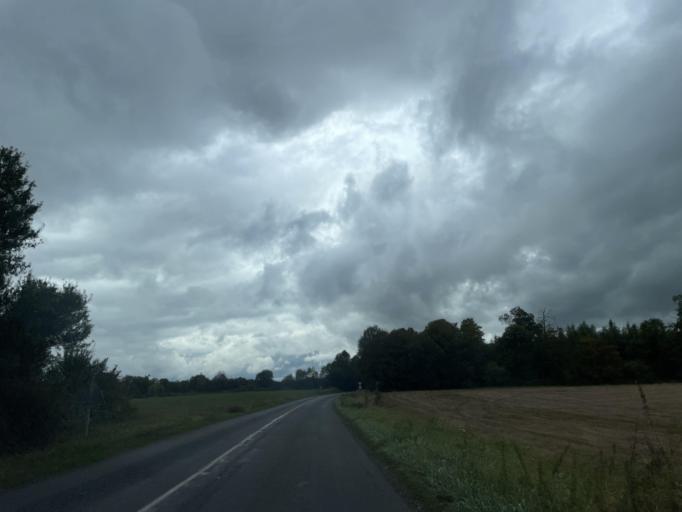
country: FR
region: Ile-de-France
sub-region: Departement de Seine-et-Marne
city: Sammeron
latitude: 48.9011
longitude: 3.0521
